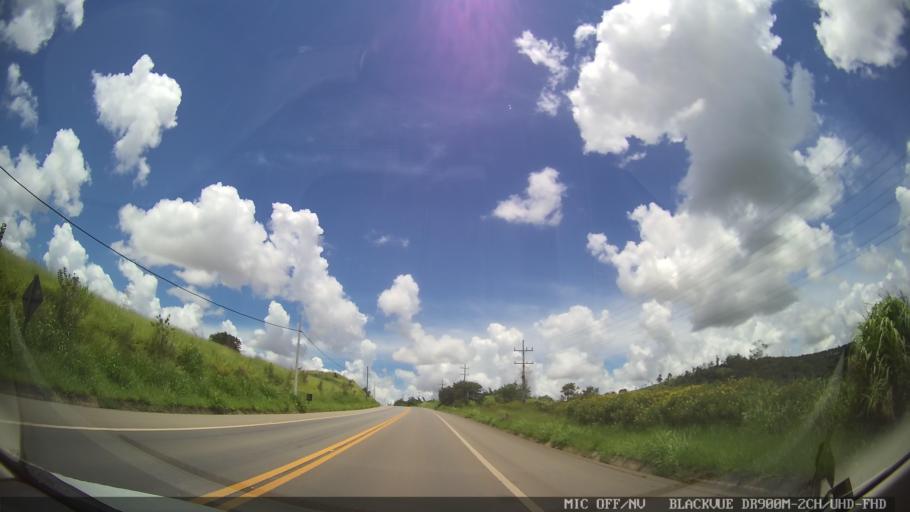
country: BR
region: Sao Paulo
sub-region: Braganca Paulista
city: Braganca Paulista
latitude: -22.9079
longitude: -46.5775
